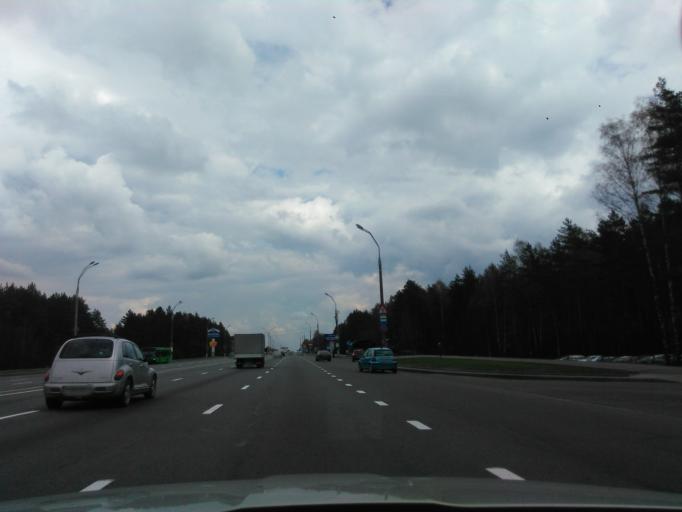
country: BY
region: Minsk
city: Lyeskawka
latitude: 53.9610
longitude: 27.7324
